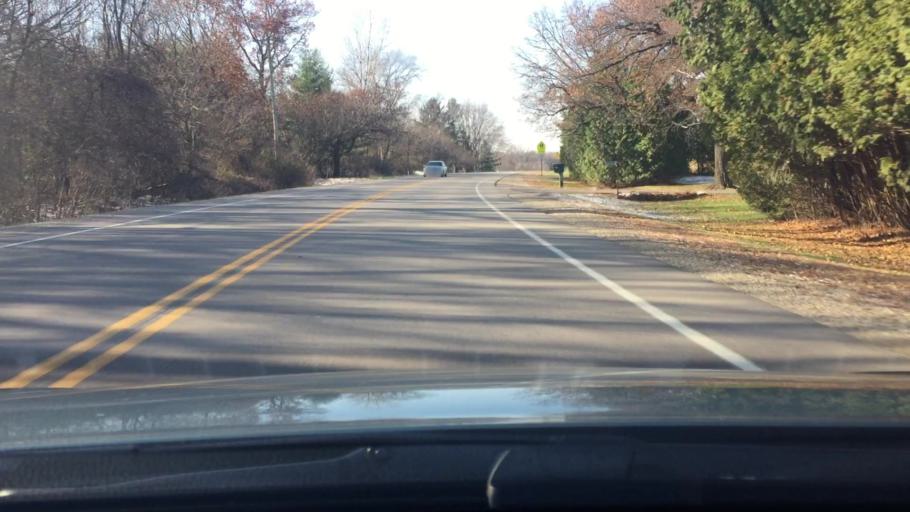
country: US
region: Wisconsin
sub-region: Jefferson County
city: Cambridge
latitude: 43.0090
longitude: -89.0044
